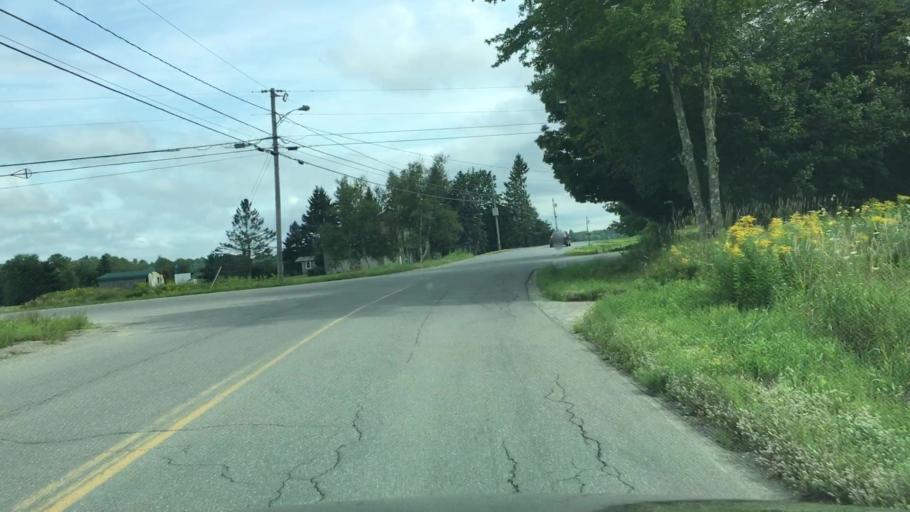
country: US
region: Maine
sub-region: Waldo County
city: Winterport
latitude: 44.6797
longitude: -68.8677
